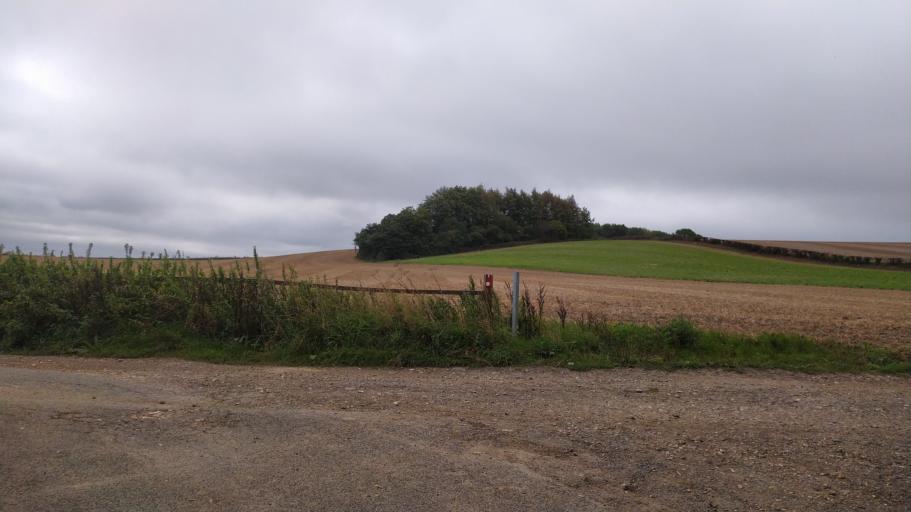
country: GB
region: England
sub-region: Hampshire
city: Long Sutton
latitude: 51.1996
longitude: -0.8884
